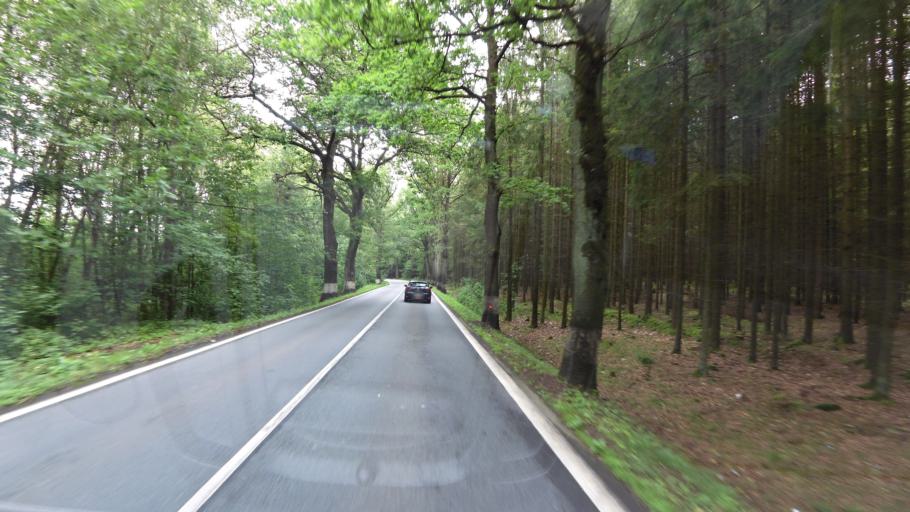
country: CZ
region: Plzensky
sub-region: Okres Domazlice
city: Klenci pod Cerchovem
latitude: 49.4130
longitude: 12.8694
